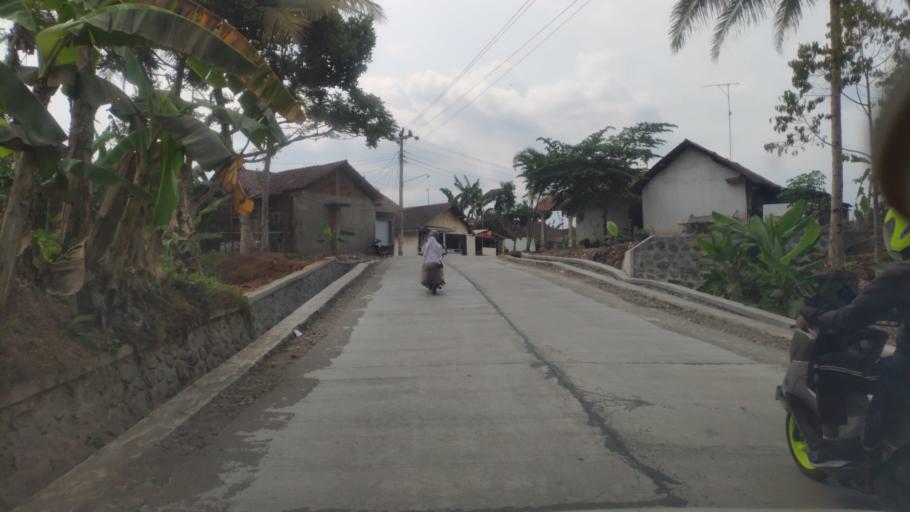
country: ID
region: Central Java
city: Wonosobo
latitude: -7.3765
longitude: 109.6657
